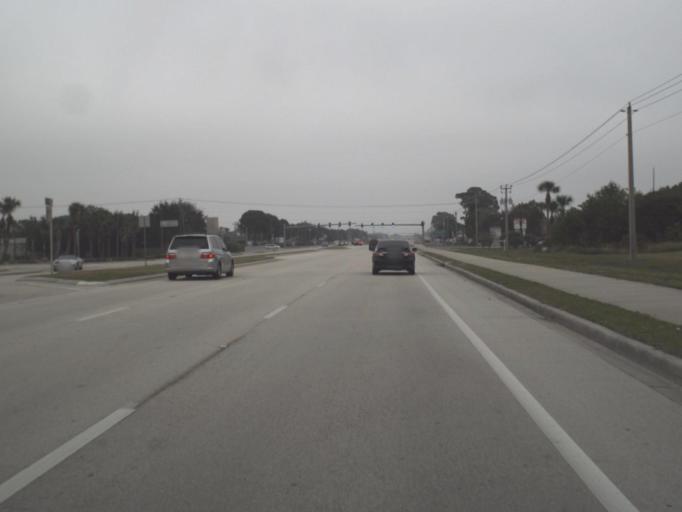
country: US
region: Florida
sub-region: Brevard County
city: Palm Bay
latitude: 28.0350
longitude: -80.6177
